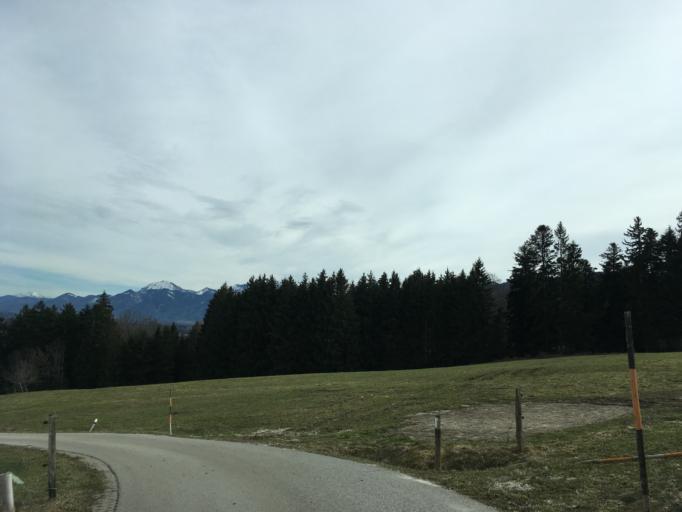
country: DE
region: Bavaria
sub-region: Upper Bavaria
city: Bernau am Chiemsee
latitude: 47.8217
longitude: 12.3486
